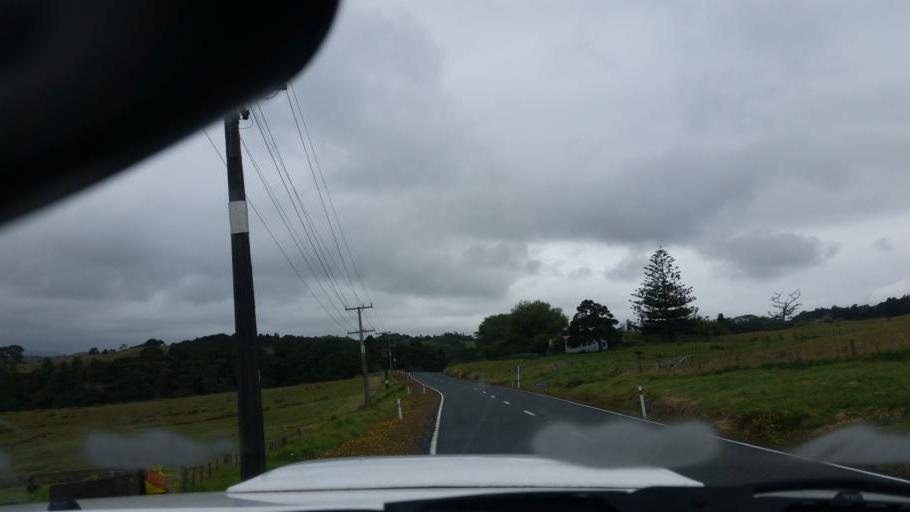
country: NZ
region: Auckland
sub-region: Auckland
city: Wellsford
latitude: -36.1578
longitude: 174.4591
